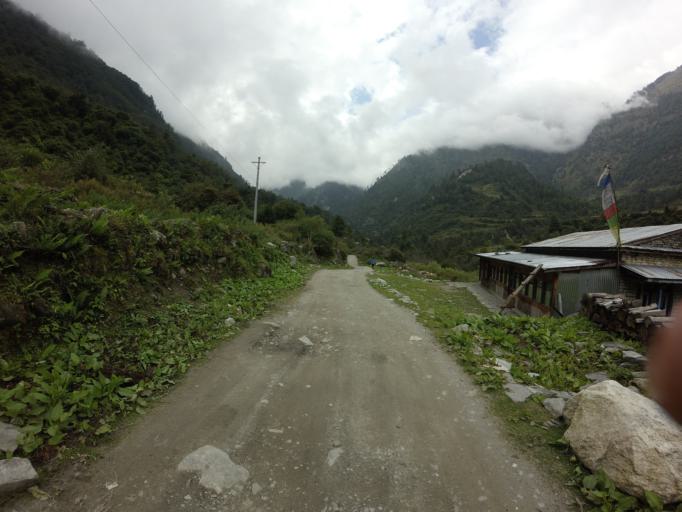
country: NP
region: Western Region
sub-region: Gandaki Zone
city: Chame
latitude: 28.5333
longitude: 84.3384
